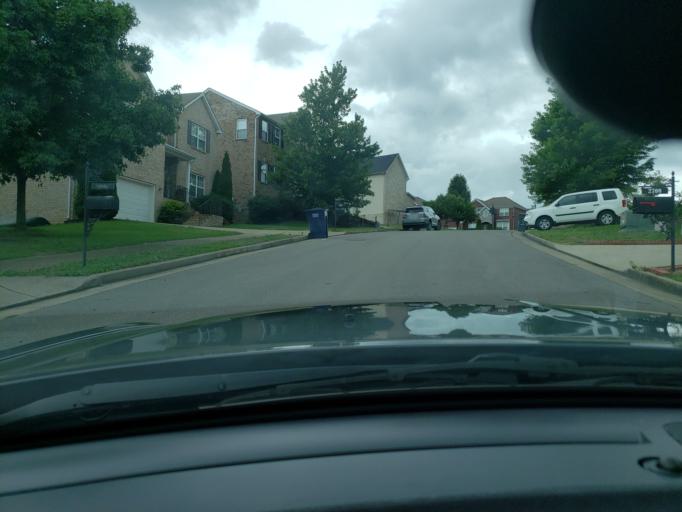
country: US
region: Tennessee
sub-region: Williamson County
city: Brentwood Estates
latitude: 36.0260
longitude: -86.7008
